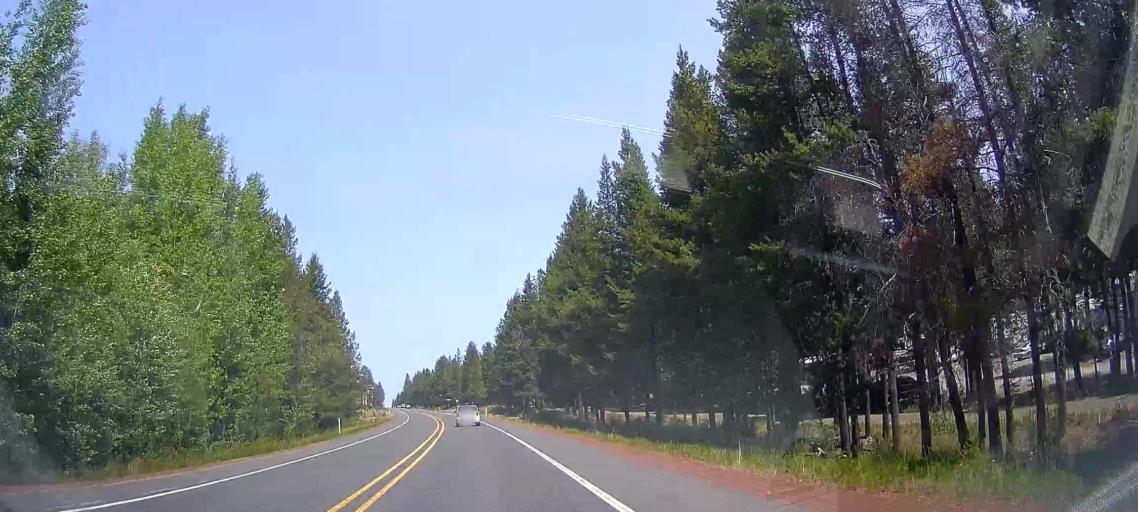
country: US
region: Oregon
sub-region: Deschutes County
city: La Pine
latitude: 43.4662
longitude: -121.6922
